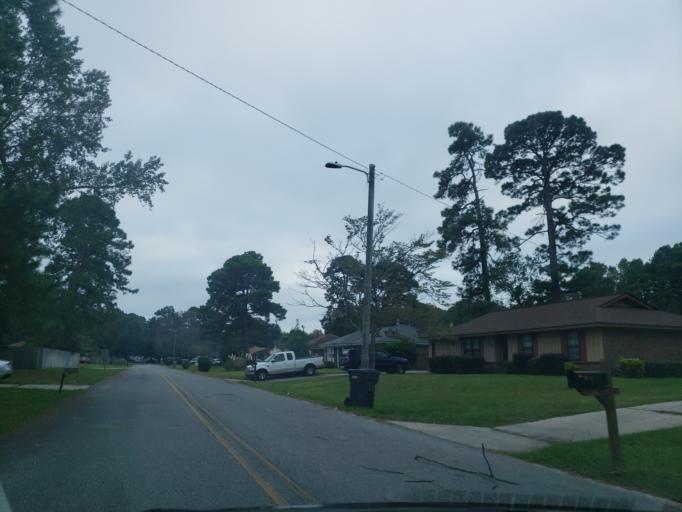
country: US
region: Georgia
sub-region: Chatham County
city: Montgomery
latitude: 31.9513
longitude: -81.1111
